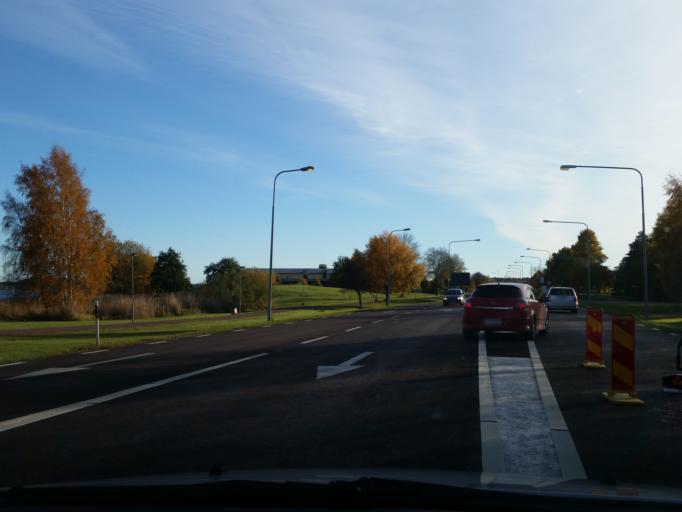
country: AX
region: Mariehamns stad
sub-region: Mariehamn
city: Mariehamn
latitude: 60.1117
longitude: 19.9429
